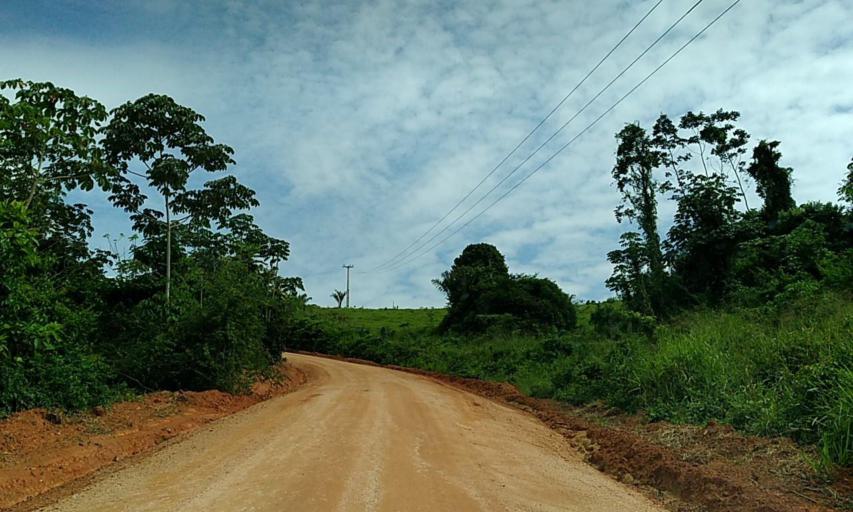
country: BR
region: Para
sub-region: Senador Jose Porfirio
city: Senador Jose Porfirio
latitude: -3.0680
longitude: -51.6348
